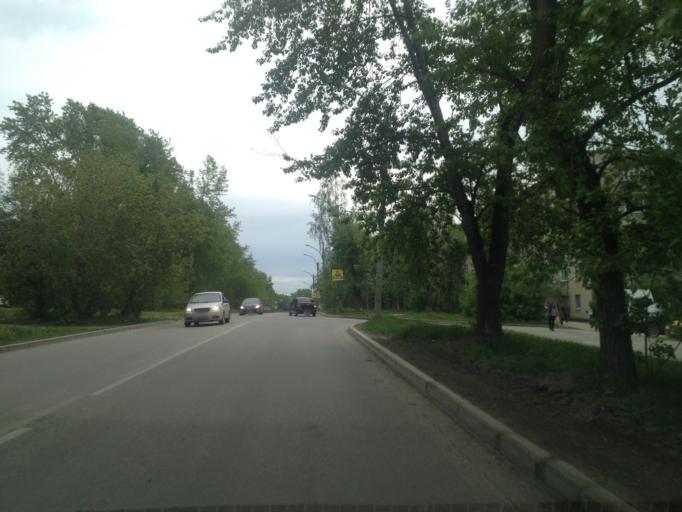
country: RU
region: Sverdlovsk
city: Sovkhoznyy
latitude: 56.7646
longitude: 60.6041
